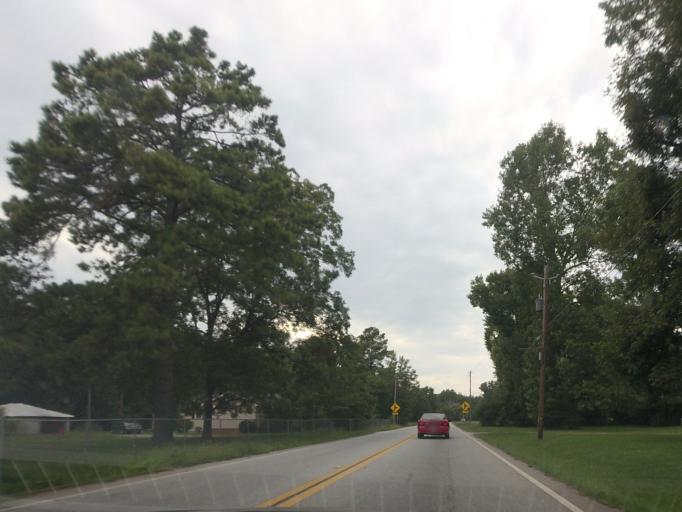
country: US
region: Georgia
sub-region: Bibb County
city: Macon
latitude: 32.8068
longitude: -83.5089
